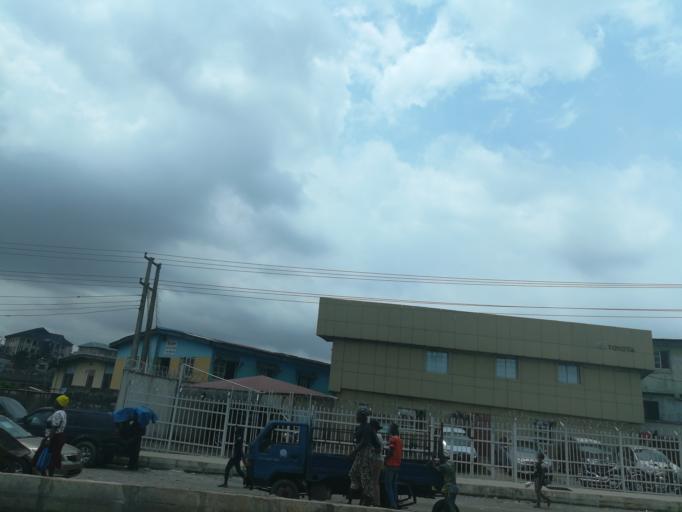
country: NG
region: Lagos
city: Ojota
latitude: 6.5715
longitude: 3.3971
